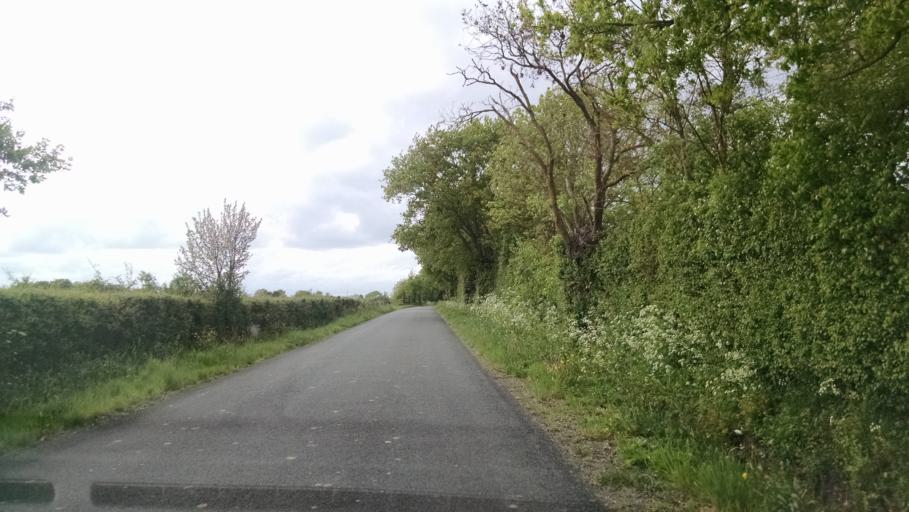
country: FR
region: Pays de la Loire
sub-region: Departement de la Vendee
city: Saint-Hilaire-de-Loulay
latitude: 46.9850
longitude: -1.3367
